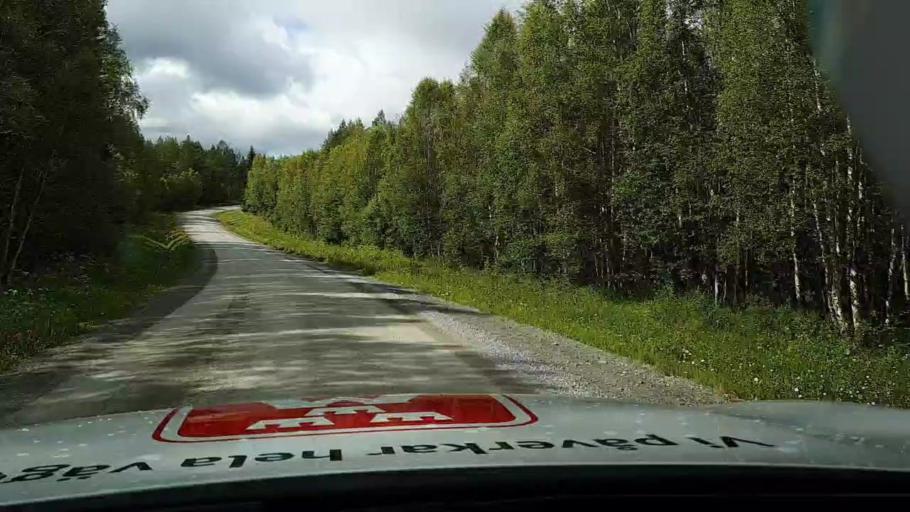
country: SE
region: Jaemtland
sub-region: Krokoms Kommun
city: Valla
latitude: 63.6497
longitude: 13.7865
